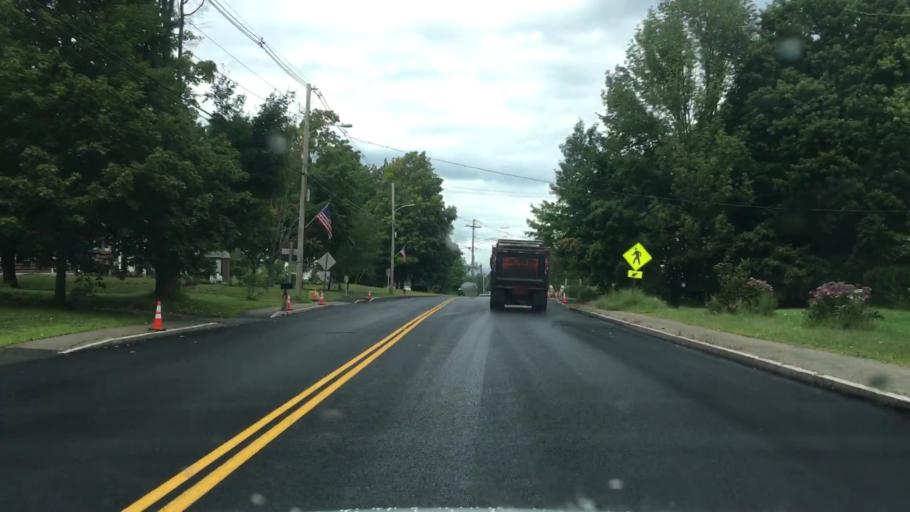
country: US
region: Maine
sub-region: York County
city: North Berwick
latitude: 43.3079
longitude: -70.7389
